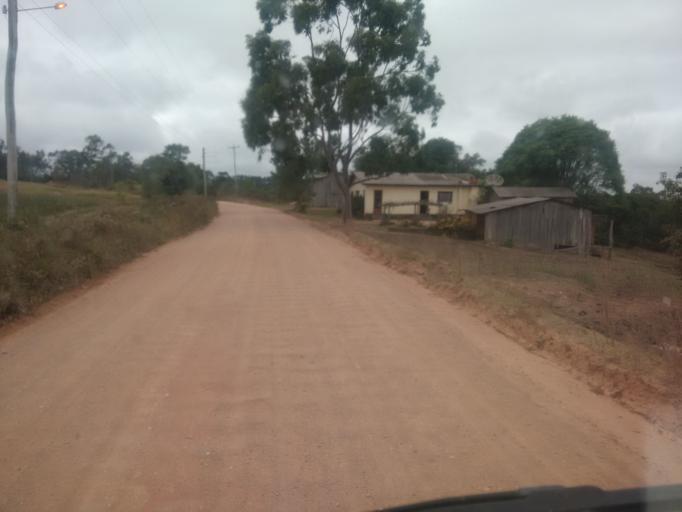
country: BR
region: Rio Grande do Sul
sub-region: Camaqua
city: Camaqua
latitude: -30.7549
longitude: -51.8842
